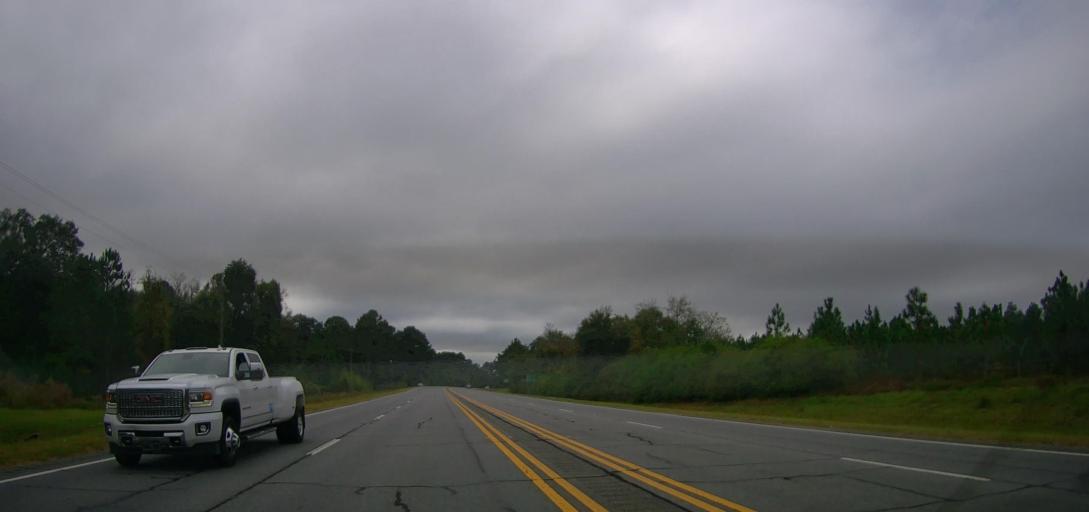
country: US
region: Georgia
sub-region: Tift County
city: Omega
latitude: 31.3091
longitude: -83.6358
